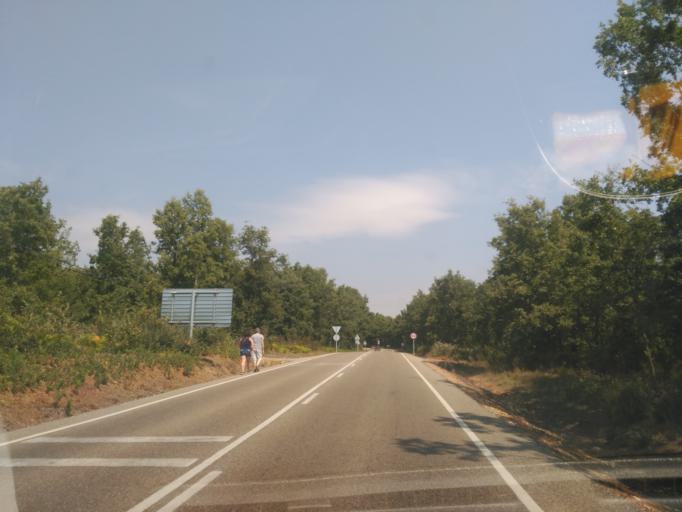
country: ES
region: Castille and Leon
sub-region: Provincia de Zamora
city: Galende
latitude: 42.0944
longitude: -6.6474
